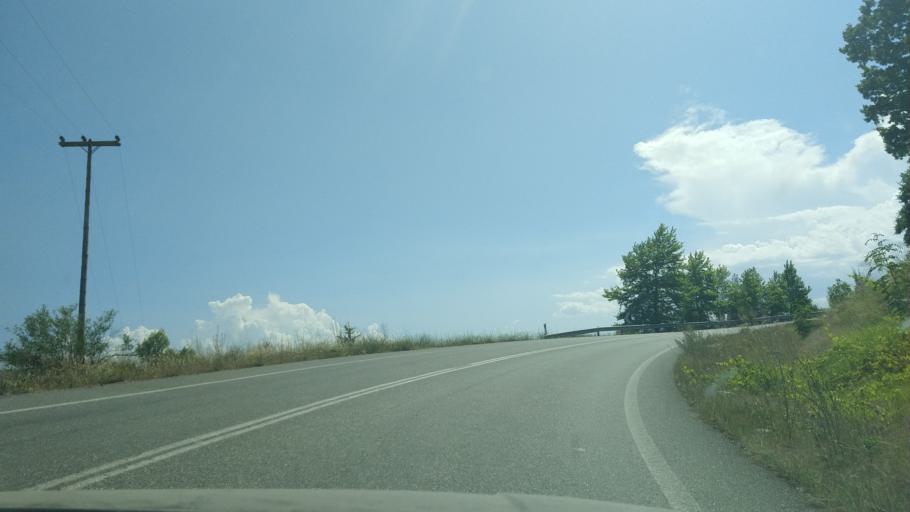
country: GR
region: West Macedonia
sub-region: Nomos Grevenon
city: Grevena
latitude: 40.0500
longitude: 21.4722
